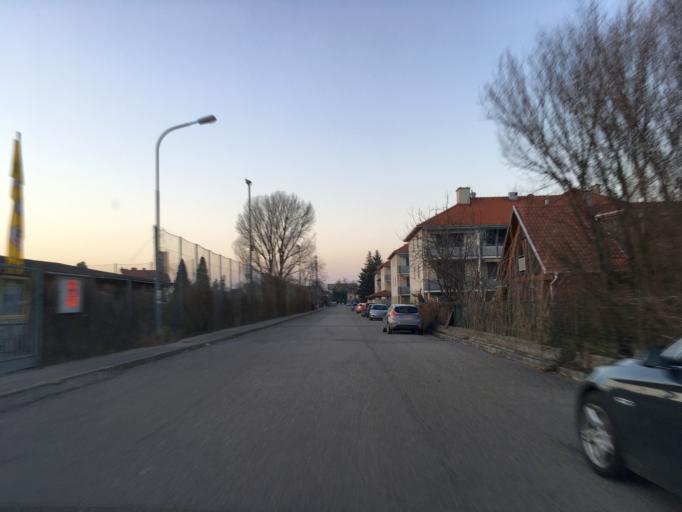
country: AT
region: Lower Austria
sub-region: Politischer Bezirk Tulln
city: Wordern
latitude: 48.3309
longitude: 16.2118
